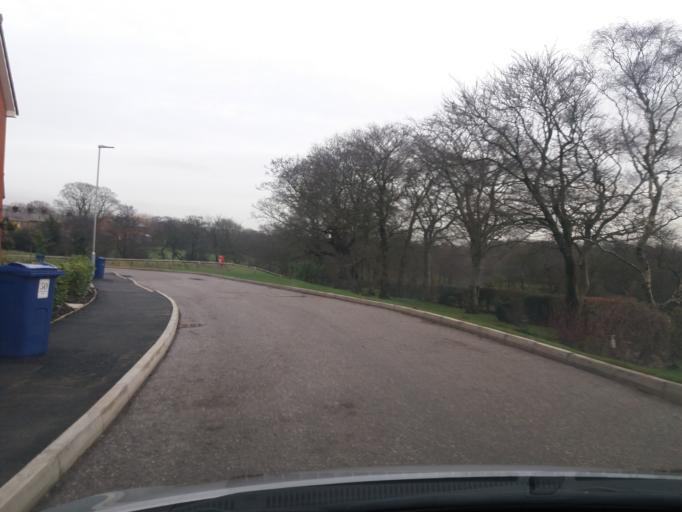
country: GB
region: England
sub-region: Lancashire
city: Adlington
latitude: 53.6121
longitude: -2.5974
